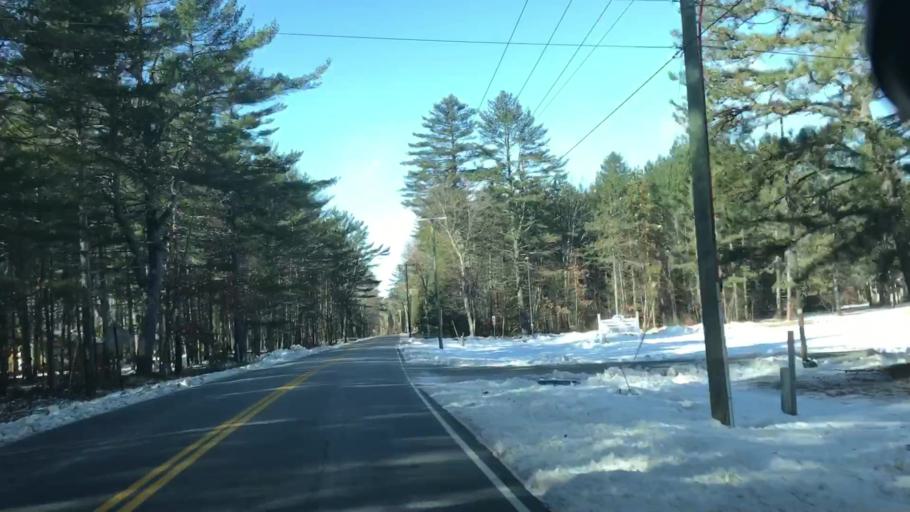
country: US
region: Maine
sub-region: Oxford County
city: Brownfield
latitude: 43.9629
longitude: -70.8611
